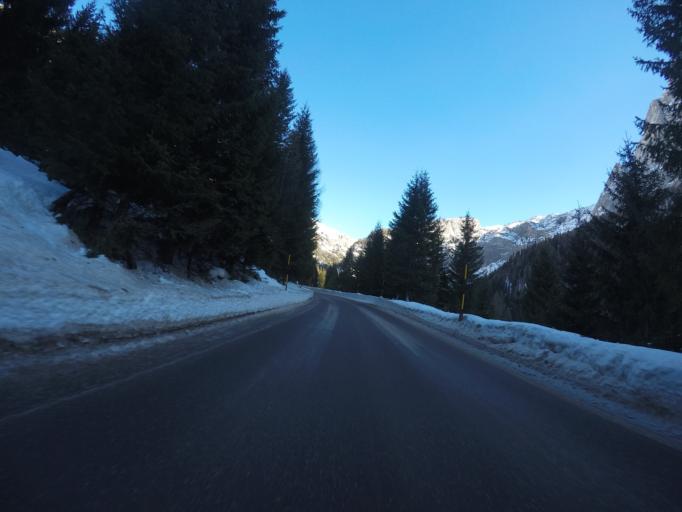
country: IT
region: Trentino-Alto Adige
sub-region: Provincia di Trento
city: Canazei
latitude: 46.4608
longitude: 11.8261
